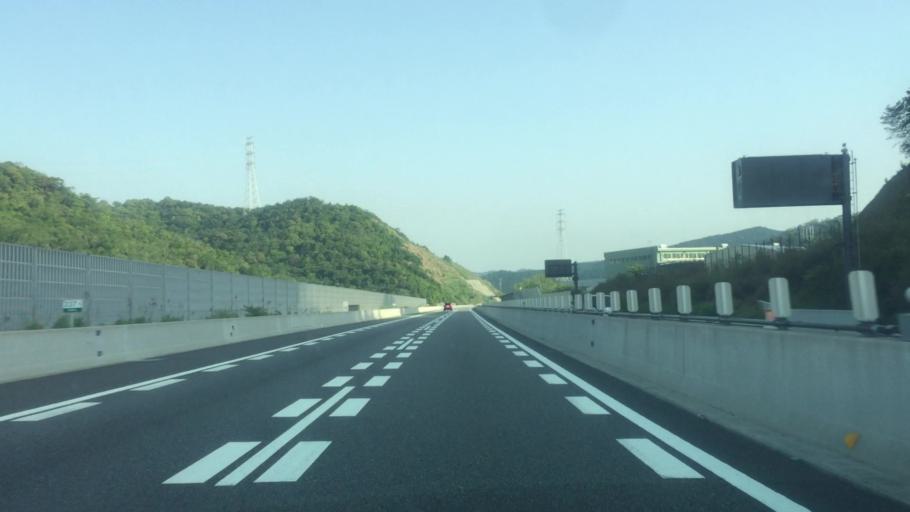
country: JP
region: Aichi
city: Gamagori
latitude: 34.9237
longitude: 137.2717
